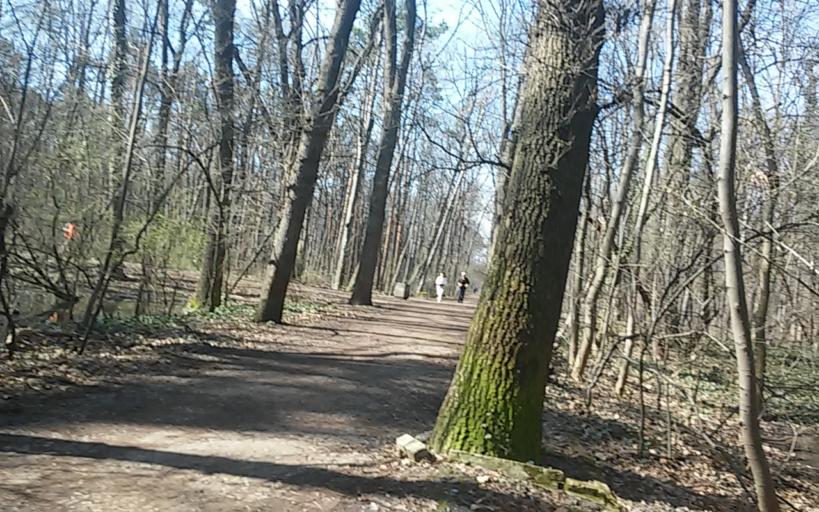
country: BG
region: Sofia-Capital
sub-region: Stolichna Obshtina
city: Sofia
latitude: 42.6798
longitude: 23.3492
